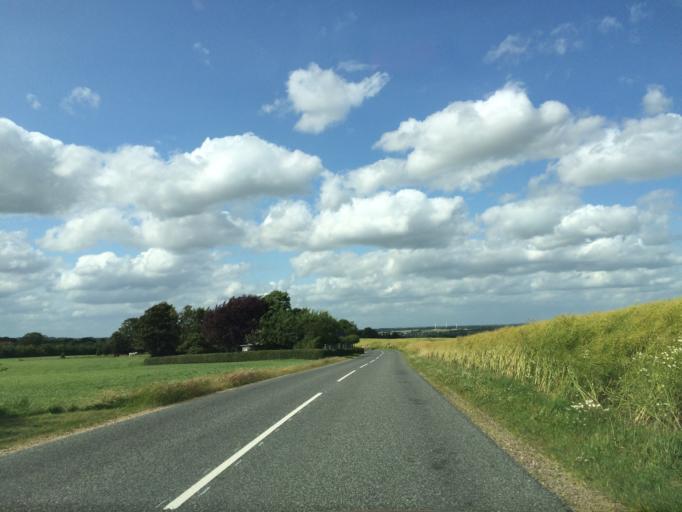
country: DK
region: Central Jutland
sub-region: Skanderborg Kommune
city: Ry
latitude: 56.2048
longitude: 9.7550
